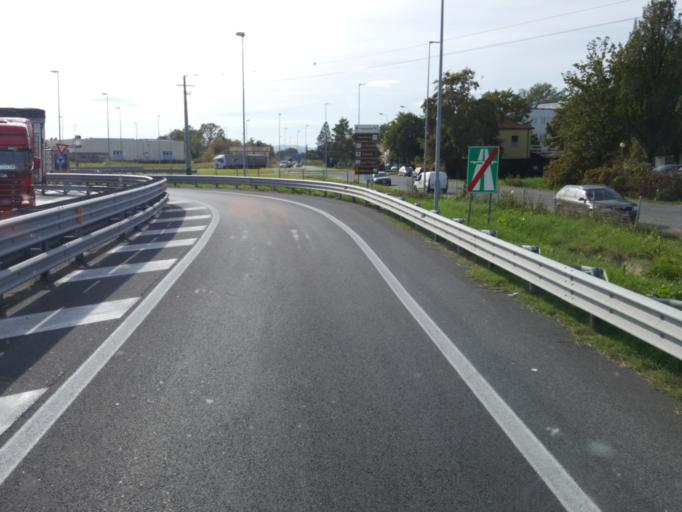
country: IT
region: Emilia-Romagna
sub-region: Provincia di Ravenna
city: Faenza
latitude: 44.3210
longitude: 11.9036
